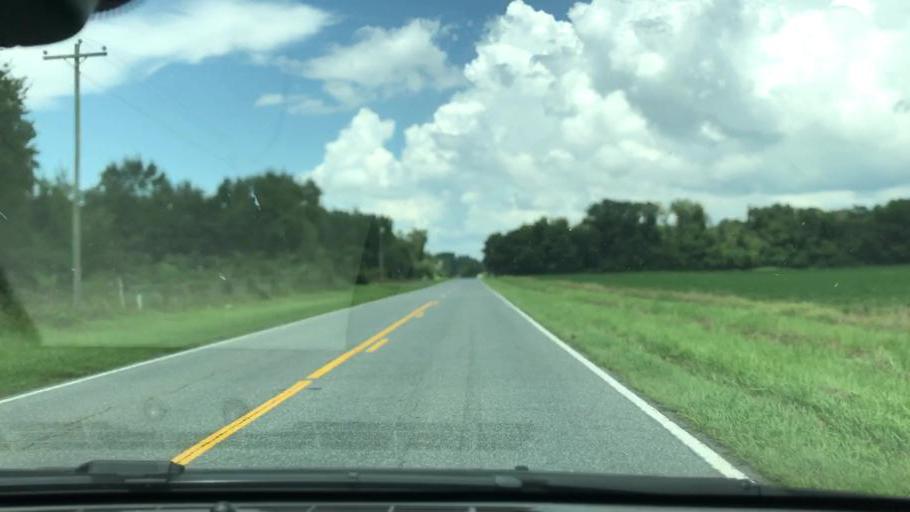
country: US
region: Florida
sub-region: Jackson County
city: Malone
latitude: 30.9528
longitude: -85.1182
